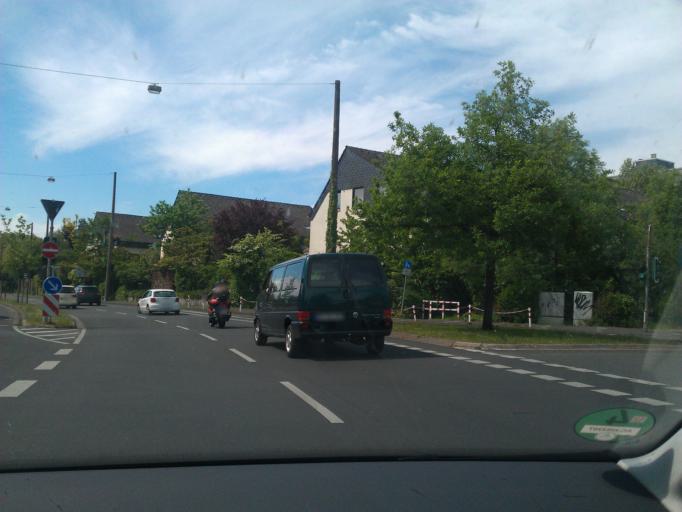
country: DE
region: North Rhine-Westphalia
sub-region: Regierungsbezirk Dusseldorf
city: Hilden
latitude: 51.1704
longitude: 6.9428
